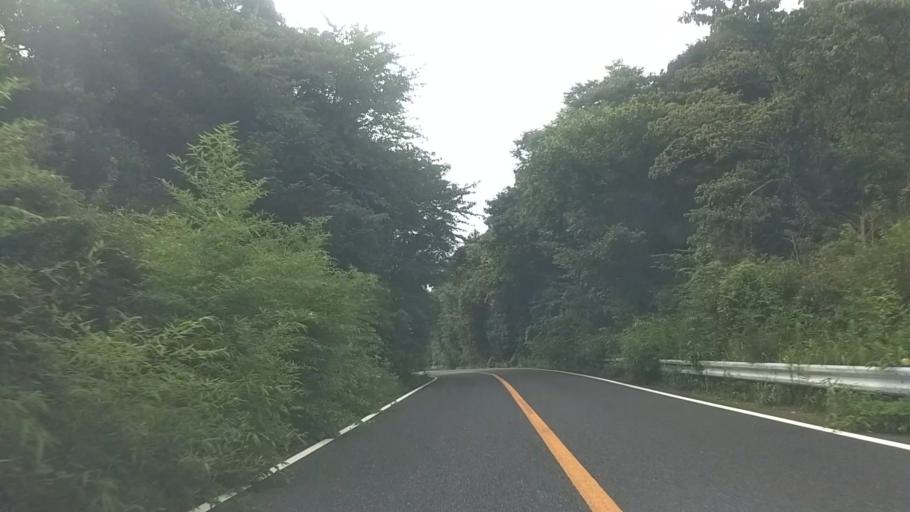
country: JP
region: Chiba
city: Kawaguchi
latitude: 35.2328
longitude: 140.0199
